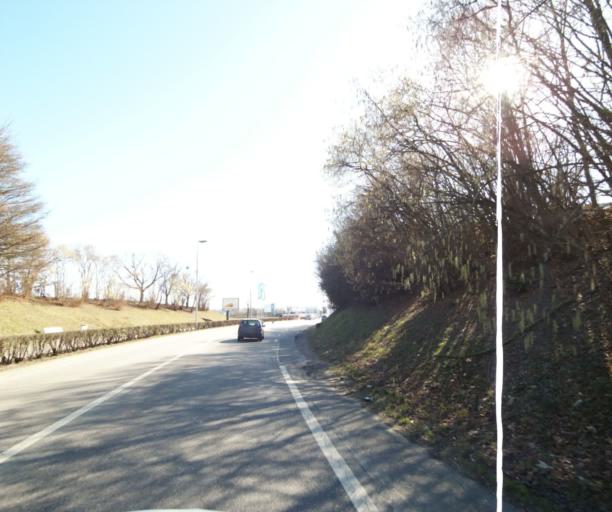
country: FR
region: Lorraine
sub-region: Departement de Meurthe-et-Moselle
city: Vandoeuvre-les-Nancy
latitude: 48.6560
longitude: 6.1787
